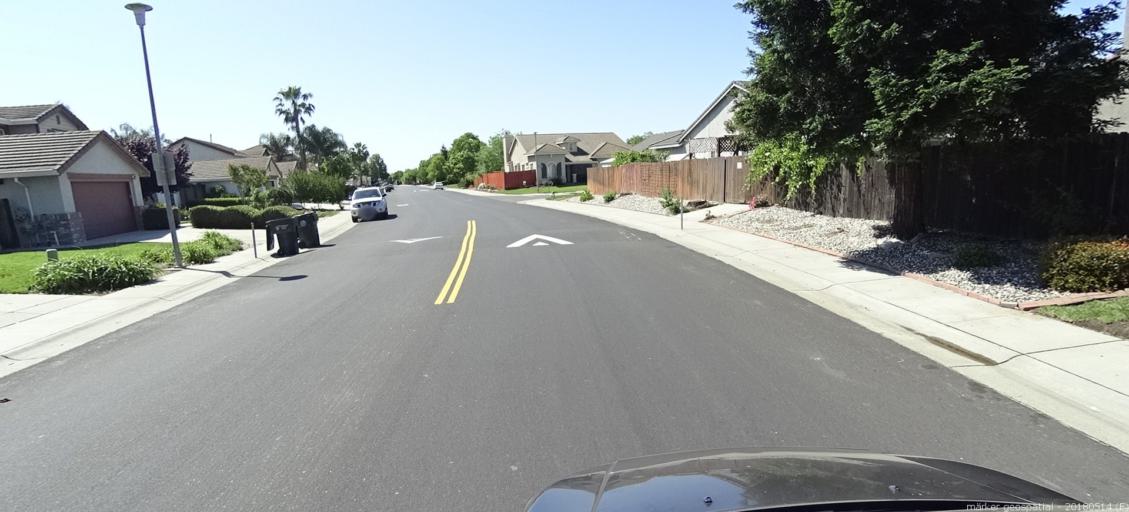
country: US
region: California
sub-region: Yolo County
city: West Sacramento
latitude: 38.6406
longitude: -121.5355
